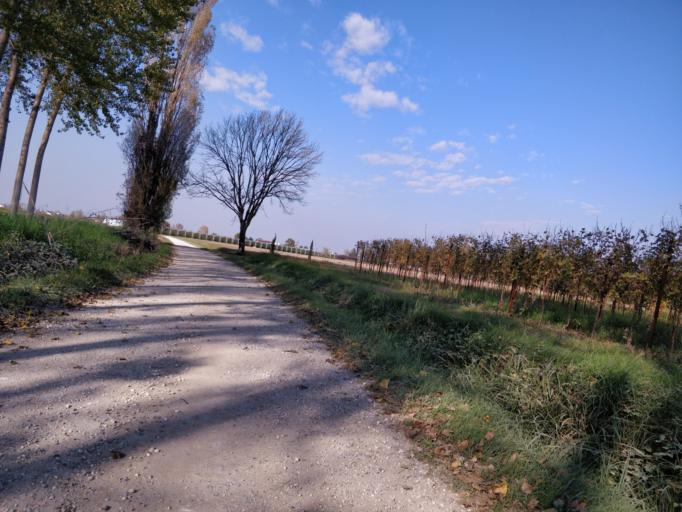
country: IT
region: Friuli Venezia Giulia
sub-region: Provincia di Udine
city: Bertiolo
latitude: 45.9339
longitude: 13.0413
